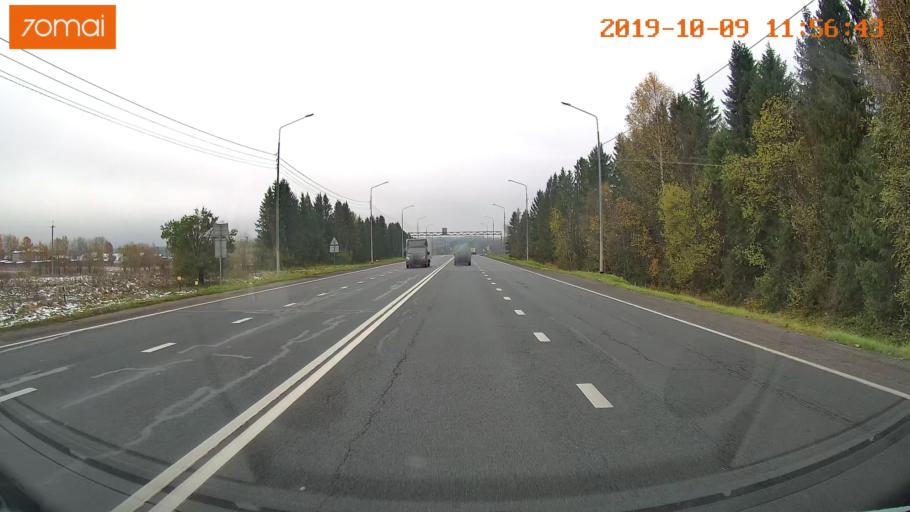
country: RU
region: Vologda
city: Gryazovets
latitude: 58.7410
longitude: 40.2889
